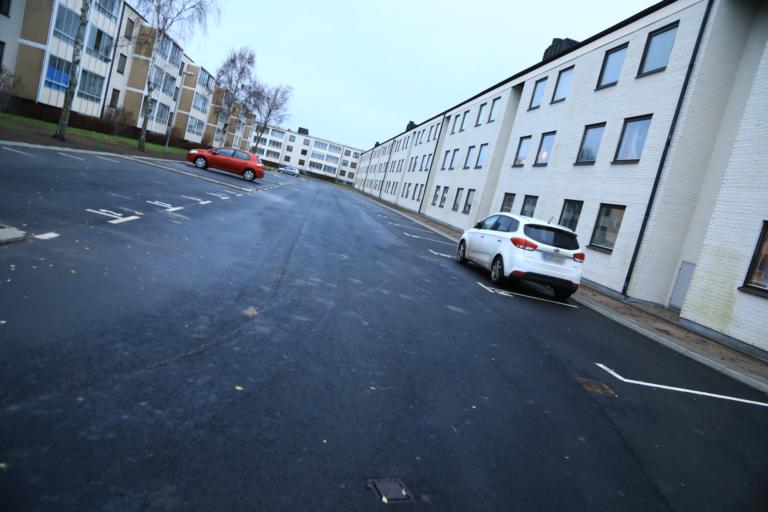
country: SE
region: Halland
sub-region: Varbergs Kommun
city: Varberg
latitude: 57.0934
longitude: 12.2620
